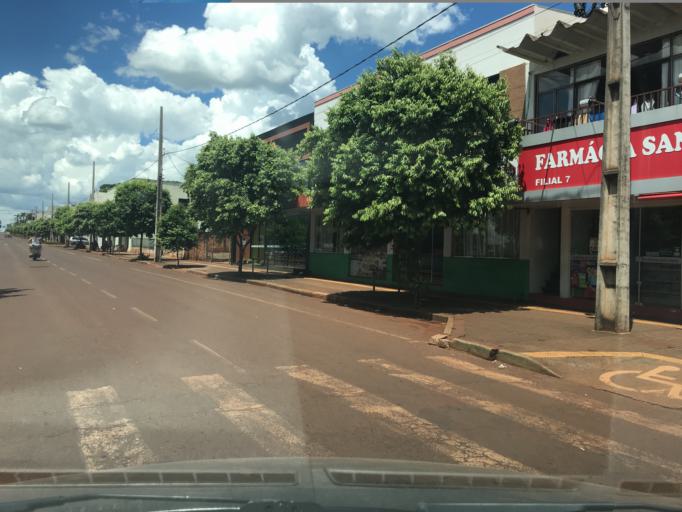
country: BR
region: Parana
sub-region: Palotina
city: Palotina
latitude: -24.2850
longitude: -53.8468
